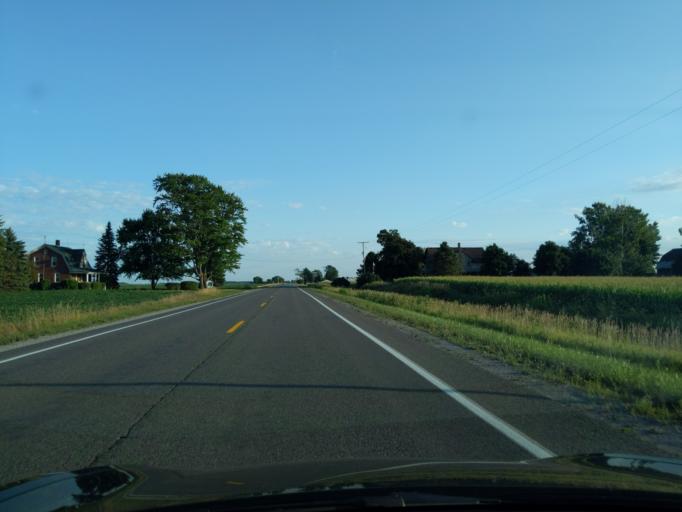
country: US
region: Michigan
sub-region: Gratiot County
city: Breckenridge
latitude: 43.5012
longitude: -84.3697
